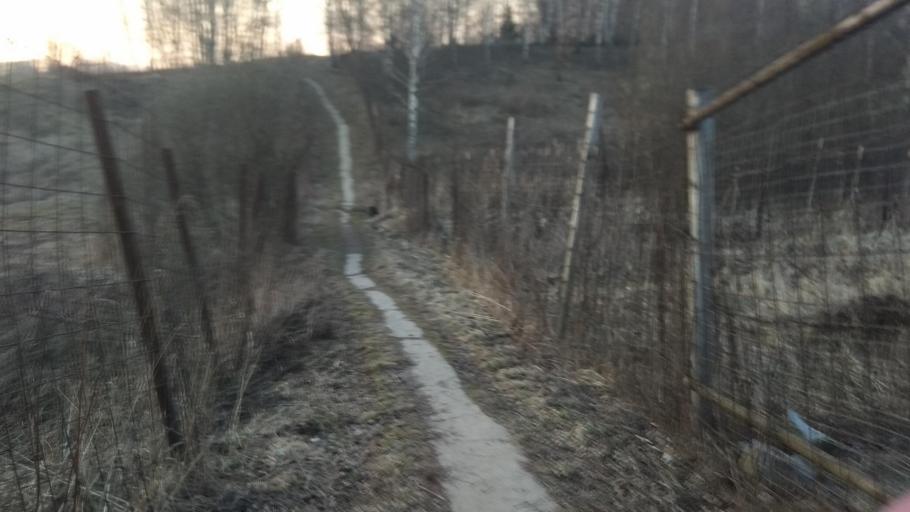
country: RU
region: Moscow
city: Zagor'ye
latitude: 55.5621
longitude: 37.6775
